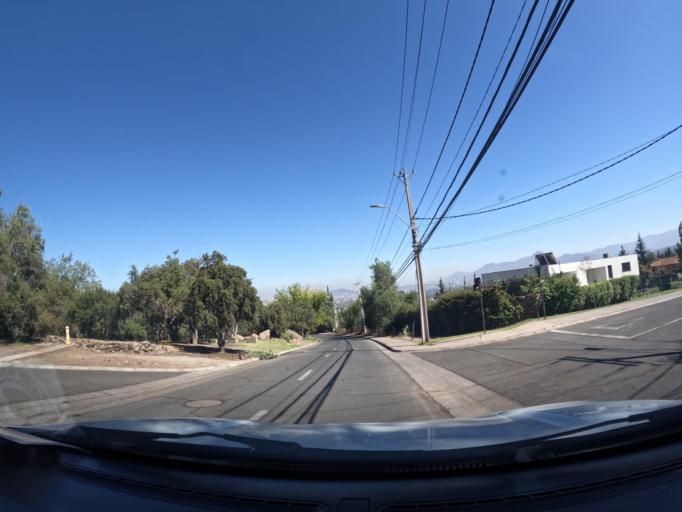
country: CL
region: Santiago Metropolitan
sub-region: Provincia de Santiago
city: Villa Presidente Frei, Nunoa, Santiago, Chile
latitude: -33.4743
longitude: -70.5215
